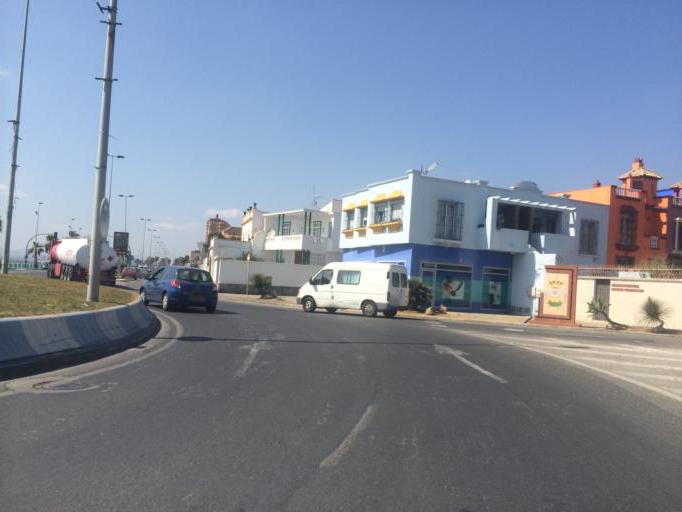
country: ES
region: Andalusia
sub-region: Provincia de Cadiz
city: La Linea de la Concepcion
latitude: 36.1670
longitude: -5.3643
